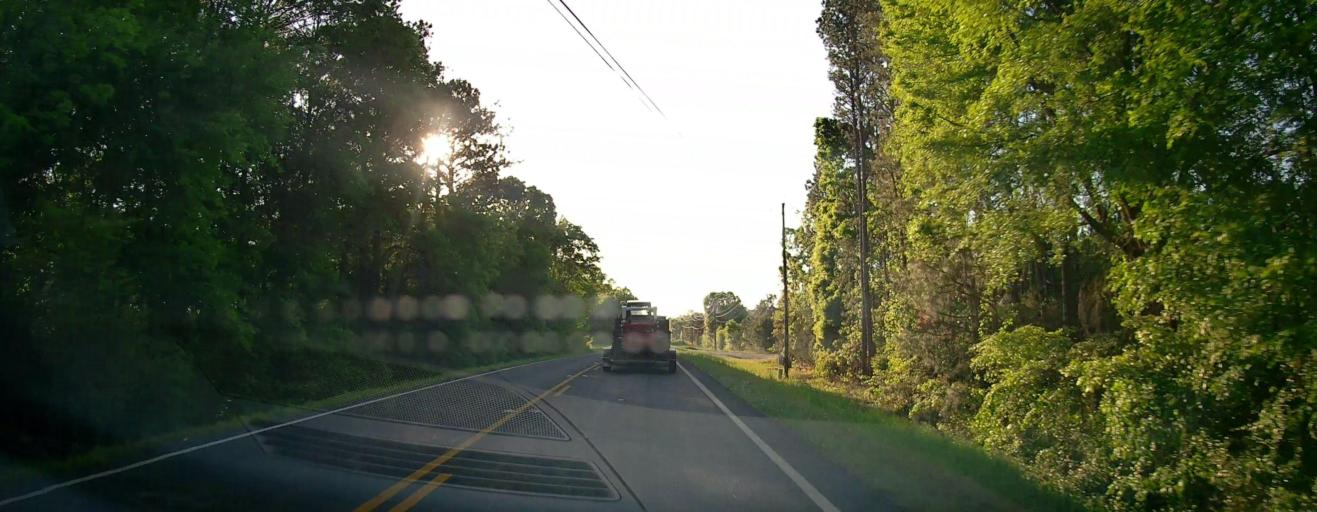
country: US
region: Georgia
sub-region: Walton County
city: Social Circle
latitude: 33.5104
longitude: -83.6822
